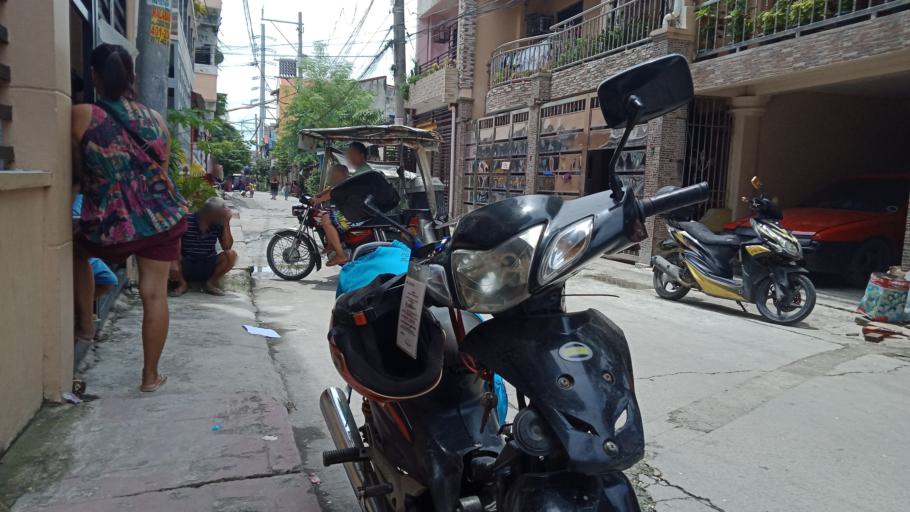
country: PH
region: Calabarzon
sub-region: Province of Rizal
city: Taytay
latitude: 14.5493
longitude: 121.1052
